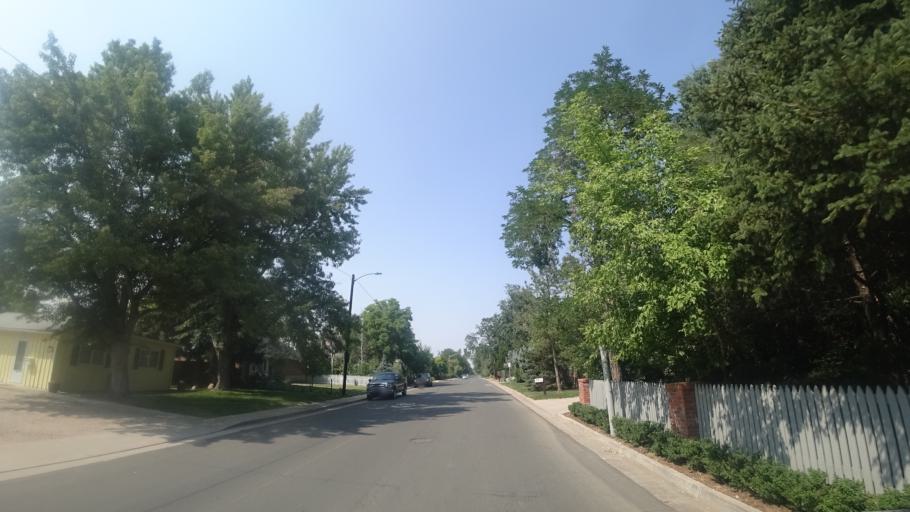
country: US
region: Colorado
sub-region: Arapahoe County
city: Englewood
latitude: 39.6355
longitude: -104.9785
